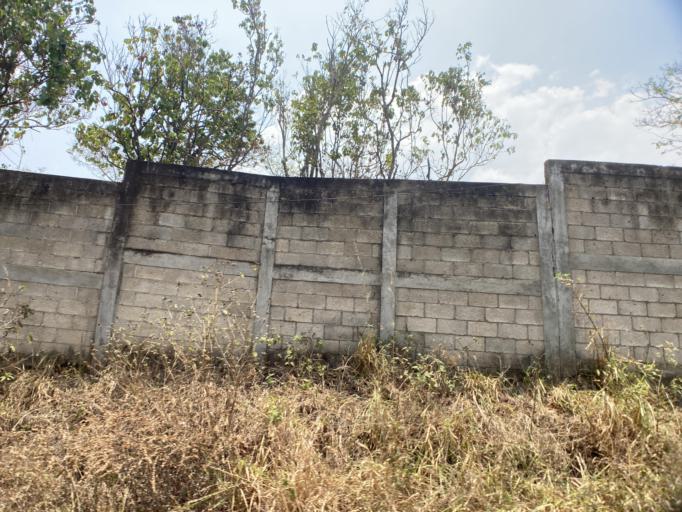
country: GT
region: Santa Rosa
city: Pueblo Nuevo Vinas
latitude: 14.3170
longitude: -90.5361
